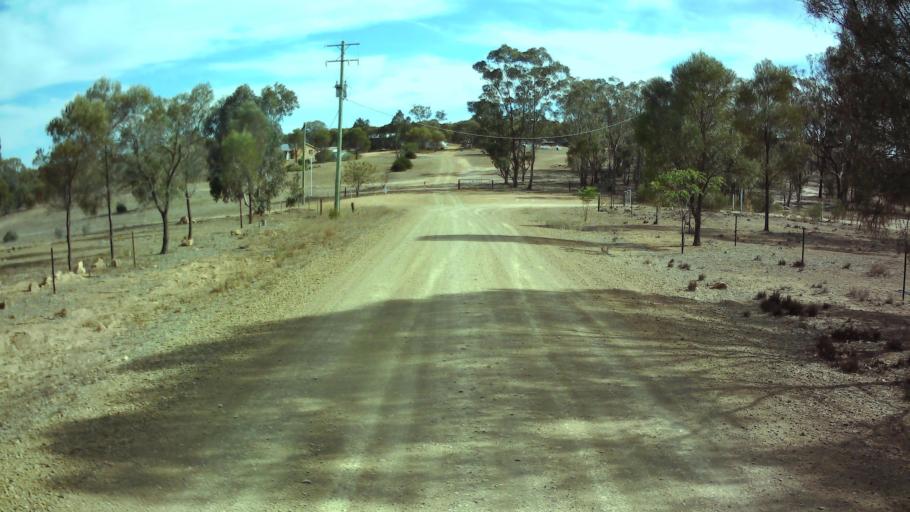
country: AU
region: New South Wales
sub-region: Weddin
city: Grenfell
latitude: -33.8705
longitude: 148.1924
